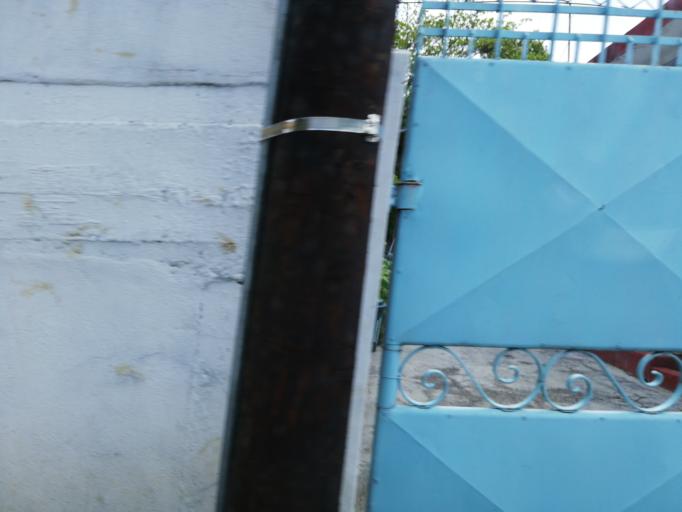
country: MU
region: Port Louis
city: Port Louis
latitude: -20.1615
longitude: 57.4822
